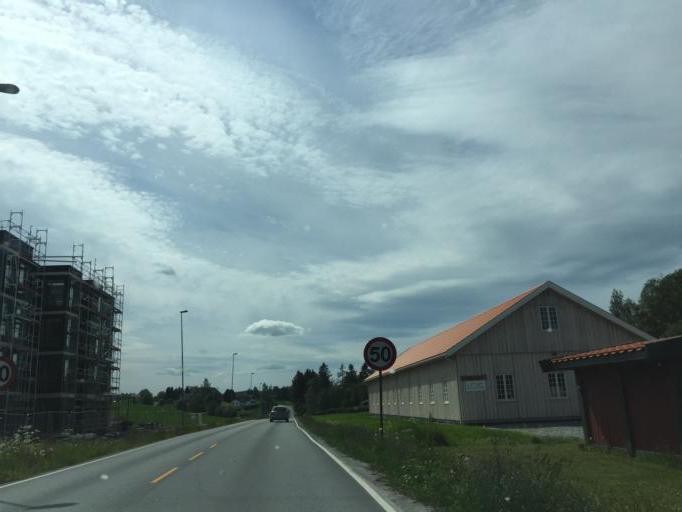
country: NO
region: Akershus
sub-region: Nes
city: Arnes
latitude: 60.1187
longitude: 11.4658
